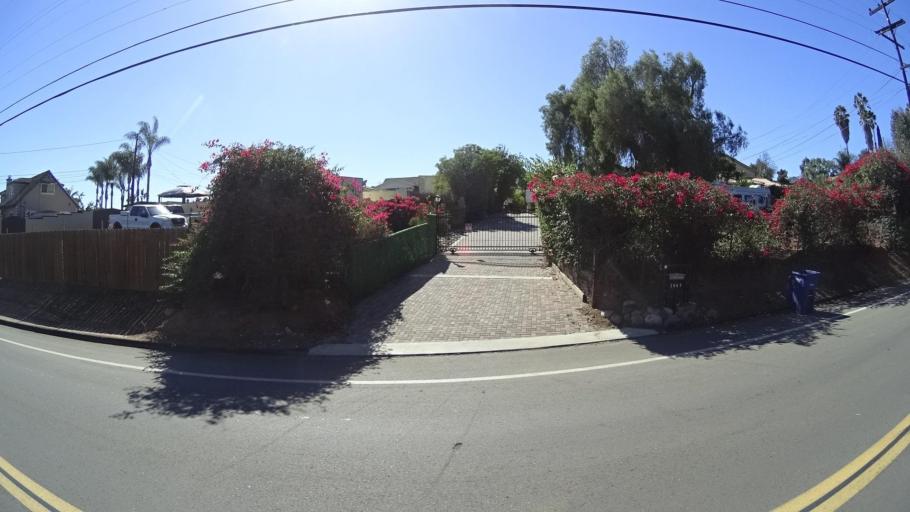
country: US
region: California
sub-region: San Diego County
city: La Presa
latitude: 32.6843
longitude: -117.0144
